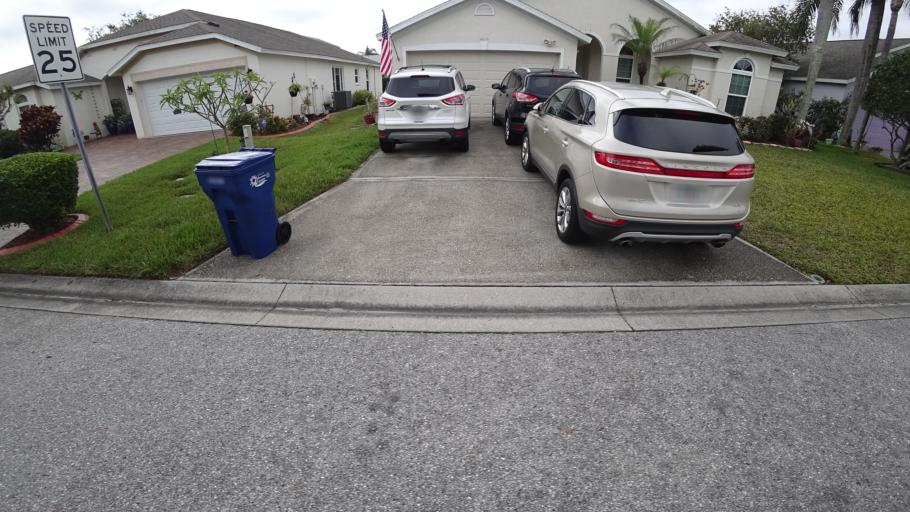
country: US
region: Florida
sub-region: Manatee County
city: South Bradenton
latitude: 27.4511
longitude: -82.6025
